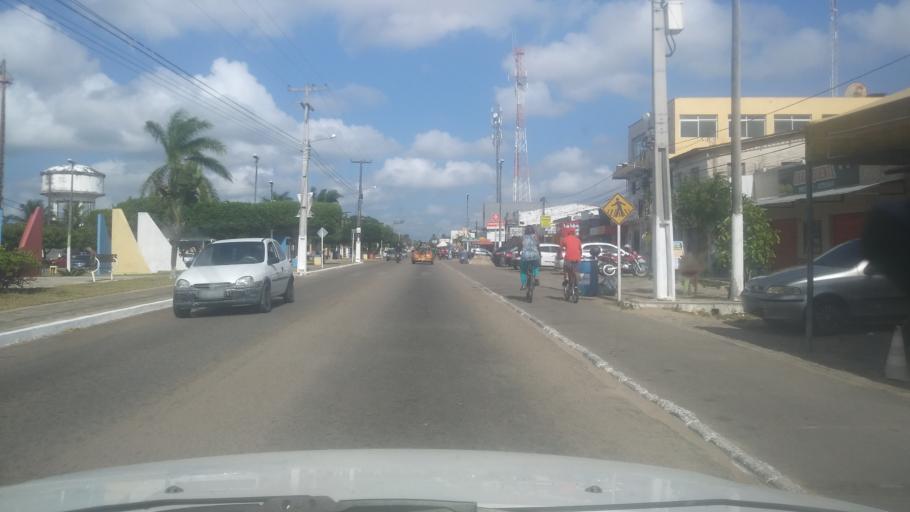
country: BR
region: Rio Grande do Norte
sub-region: Extremoz
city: Extremoz
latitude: -5.7039
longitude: -35.2904
